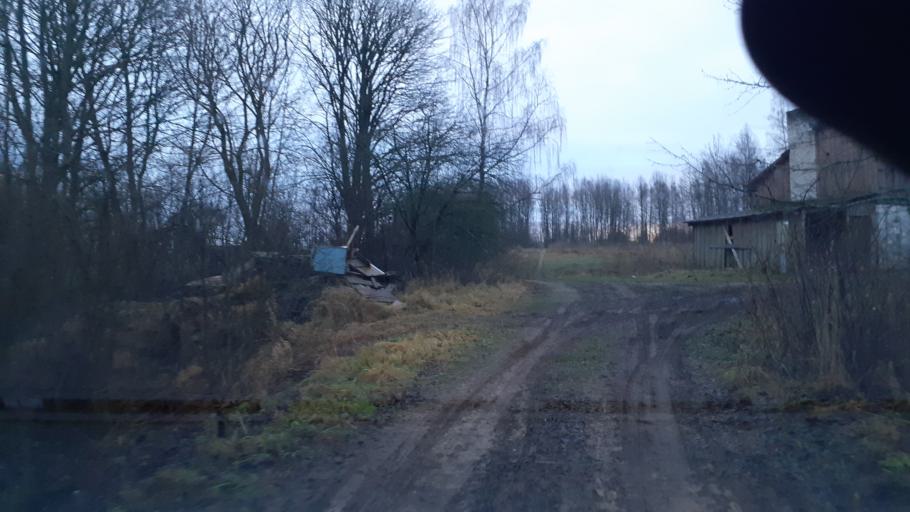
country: LV
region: Alsunga
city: Alsunga
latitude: 56.9029
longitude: 21.7025
